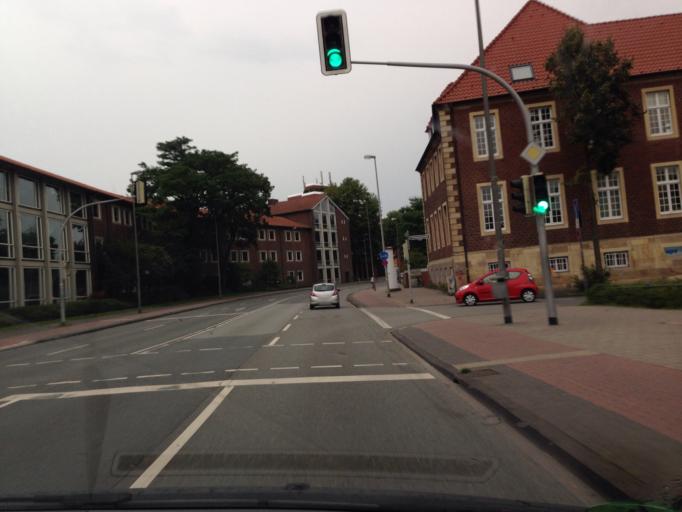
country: DE
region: North Rhine-Westphalia
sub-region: Regierungsbezirk Munster
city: Muenster
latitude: 51.9594
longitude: 7.6188
